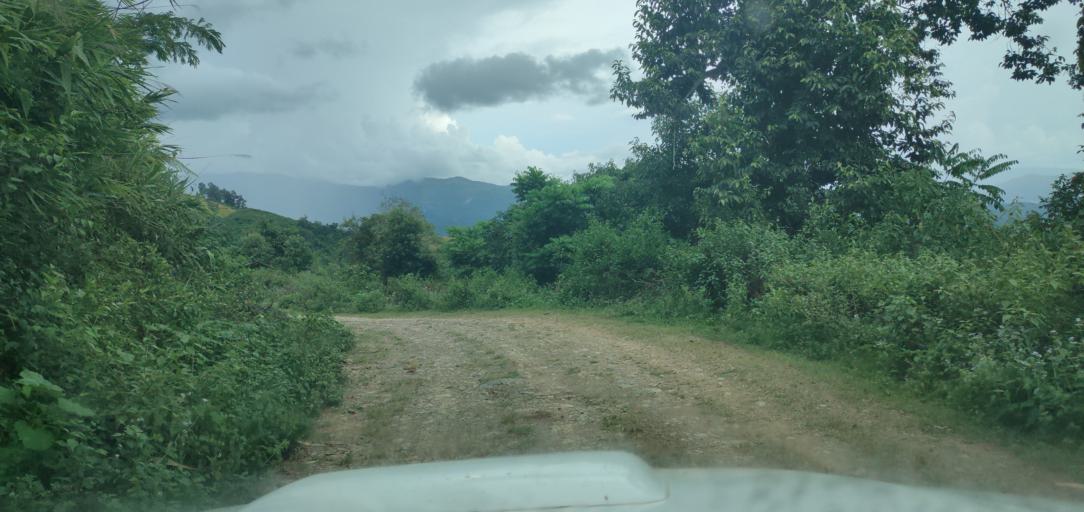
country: LA
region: Phongsali
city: Phongsali
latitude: 21.4471
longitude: 102.3094
